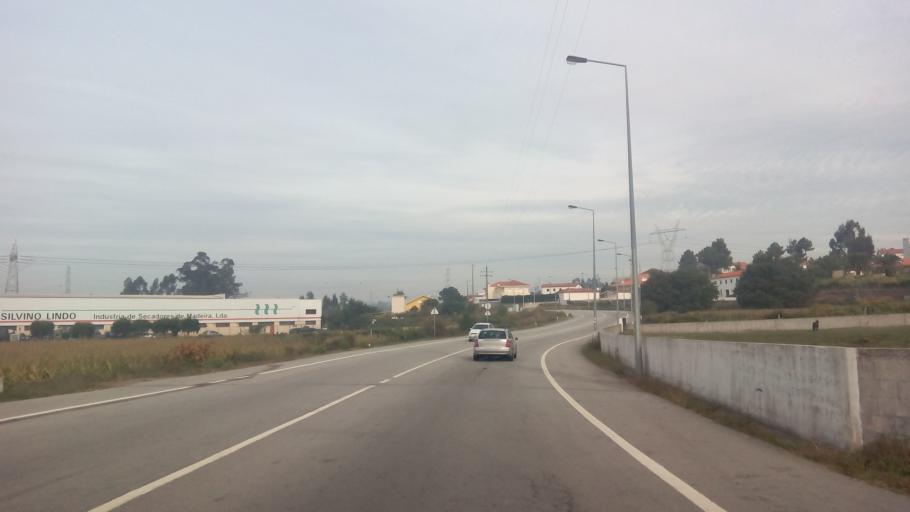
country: PT
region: Porto
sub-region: Paredes
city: Gandra
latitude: 41.1965
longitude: -8.4341
